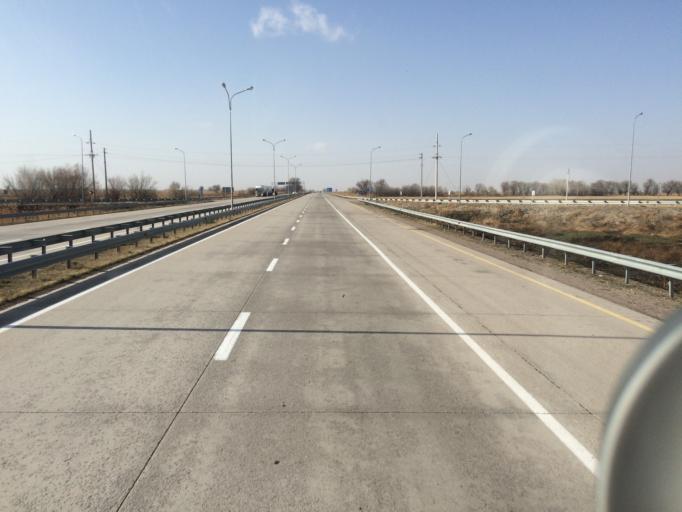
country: KZ
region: Zhambyl
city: Oytal
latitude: 42.9288
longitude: 73.2405
